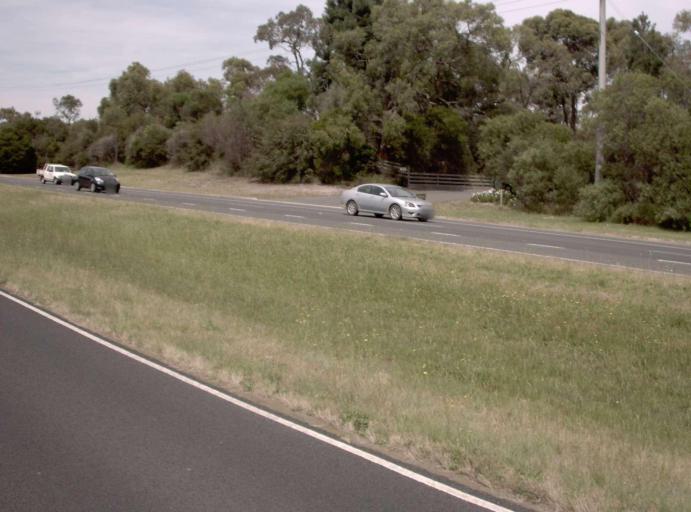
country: AU
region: Victoria
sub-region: Casey
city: Cranbourne South
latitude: -38.1276
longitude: 145.2296
